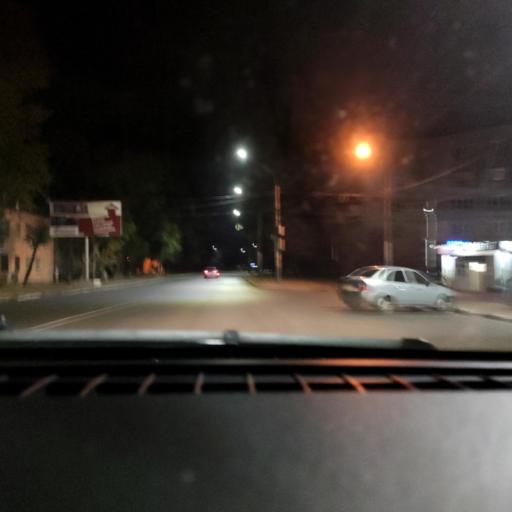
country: RU
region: Voronezj
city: Somovo
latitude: 51.7201
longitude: 39.2717
